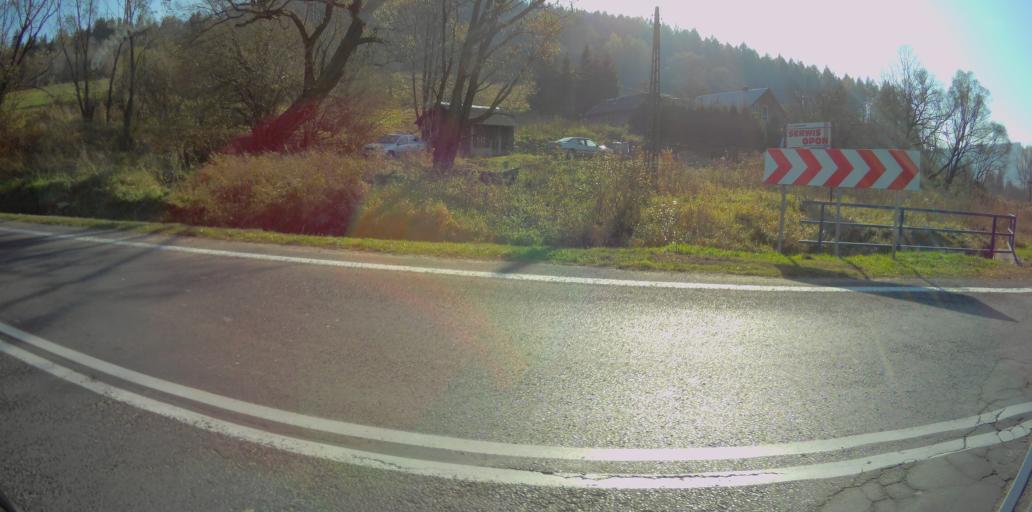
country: PL
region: Subcarpathian Voivodeship
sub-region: Powiat bieszczadzki
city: Ustrzyki Dolne
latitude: 49.4379
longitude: 22.6051
